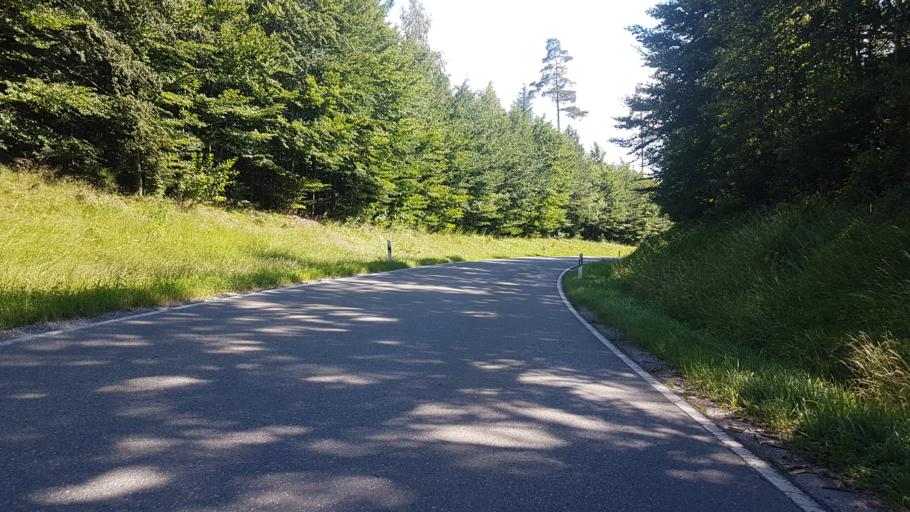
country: DE
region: Baden-Wuerttemberg
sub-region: Freiburg Region
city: Konigsfeld im Schwarzwald
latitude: 48.1386
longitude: 8.4079
